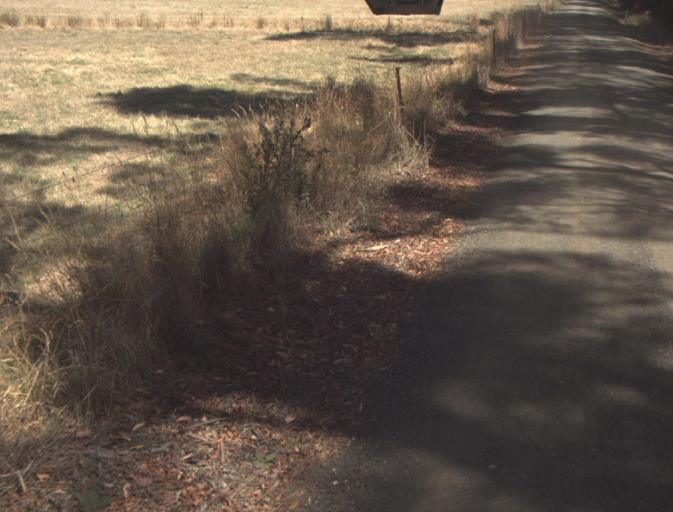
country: AU
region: Tasmania
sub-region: Launceston
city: Mayfield
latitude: -41.2607
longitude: 147.1487
